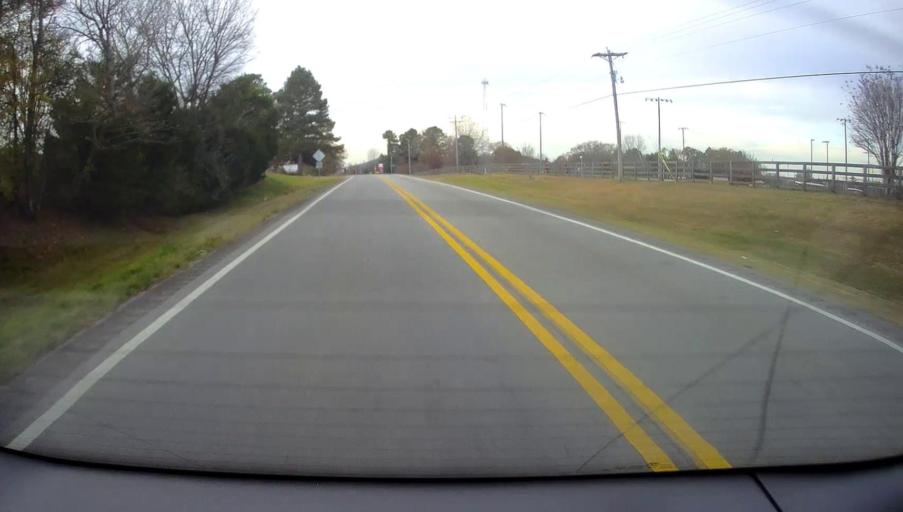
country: US
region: Alabama
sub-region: Morgan County
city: Falkville
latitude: 34.4136
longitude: -86.7006
